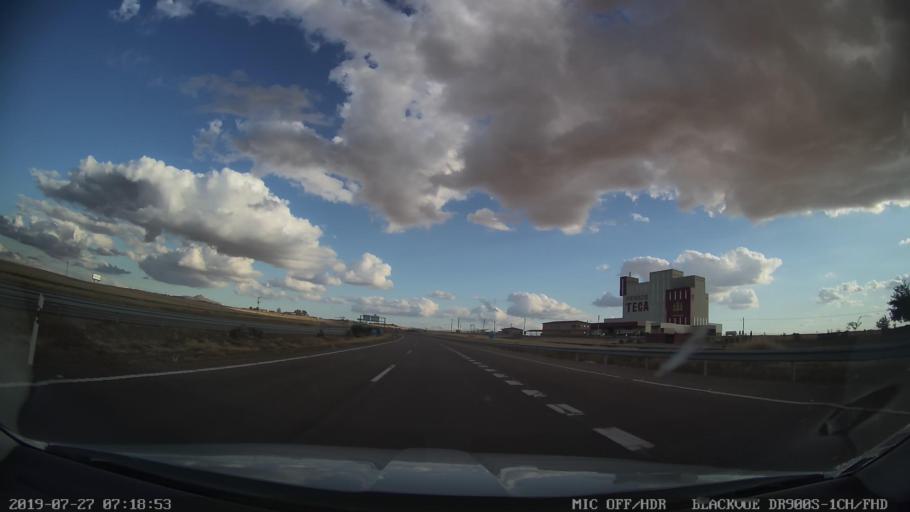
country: ES
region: Extremadura
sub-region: Provincia de Caceres
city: Trujillo
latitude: 39.4091
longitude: -5.8892
